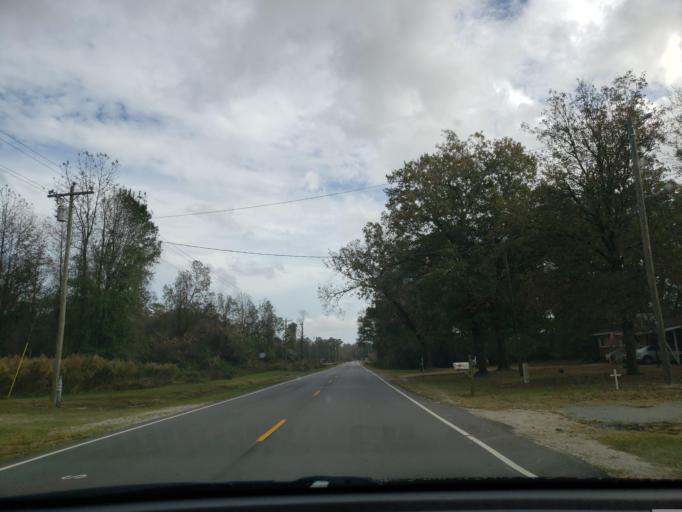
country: US
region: North Carolina
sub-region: Duplin County
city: Beulaville
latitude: 34.8361
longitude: -77.8578
